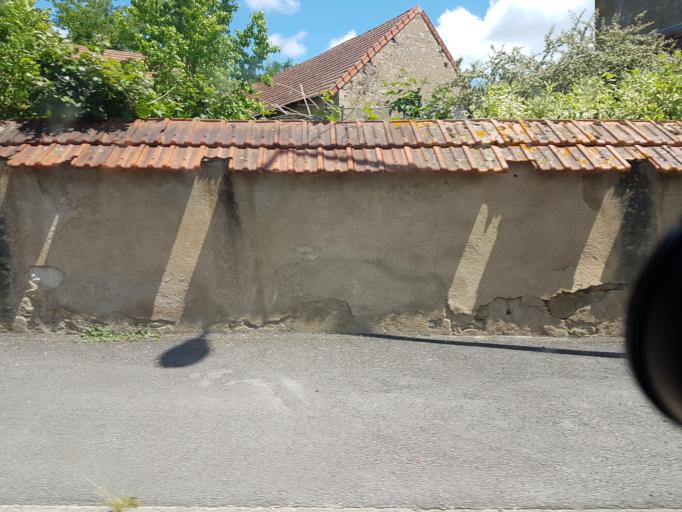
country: FR
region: Bourgogne
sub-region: Departement de Saone-et-Loire
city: Curgy
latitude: 47.0163
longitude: 4.4469
